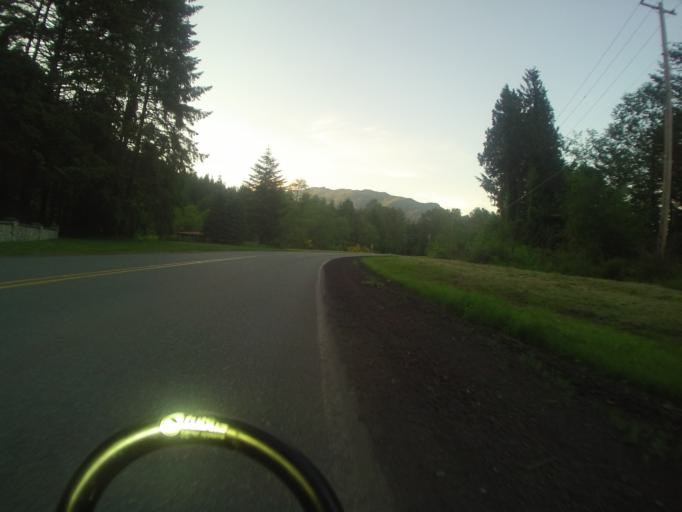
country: CA
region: British Columbia
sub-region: Fraser Valley Regional District
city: Chilliwack
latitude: 49.2826
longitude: -121.9485
